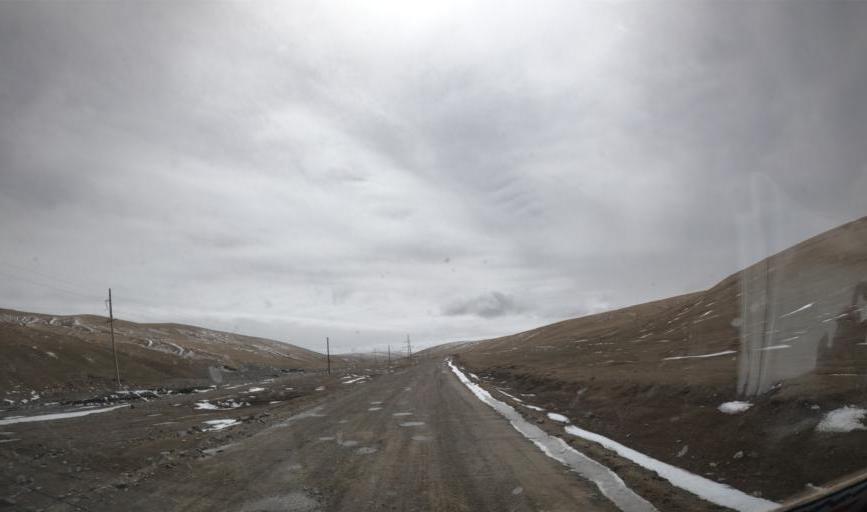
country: KG
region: Naryn
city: Naryn
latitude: 41.0795
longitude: 76.4434
